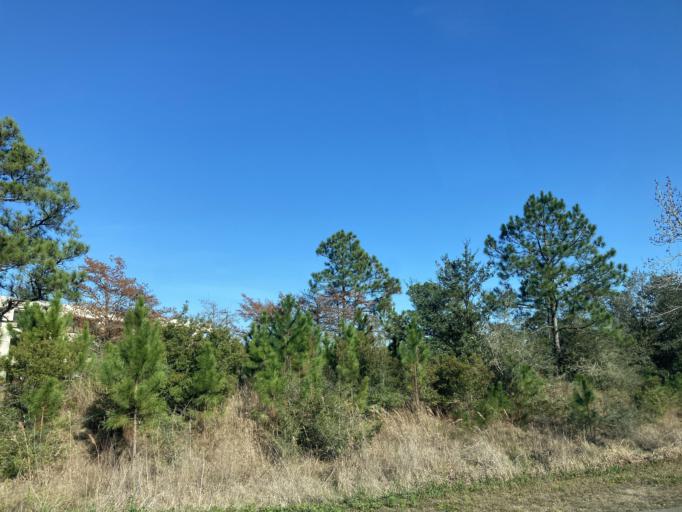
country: US
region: Mississippi
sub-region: Harrison County
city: West Gulfport
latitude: 30.4324
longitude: -89.0562
